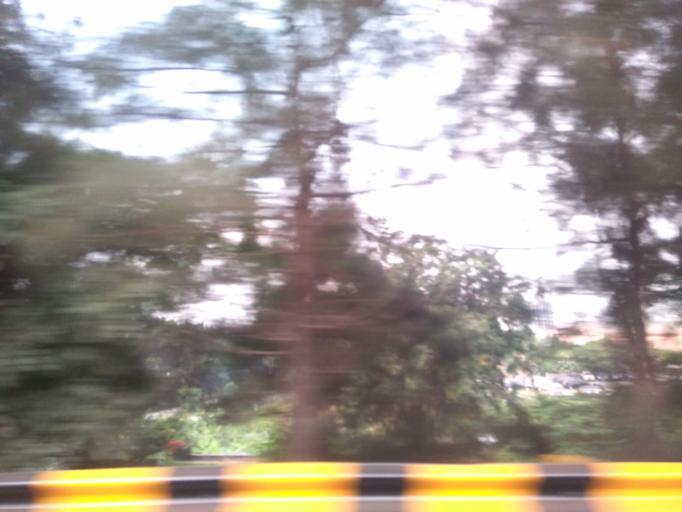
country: ID
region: West Java
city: Bekasi
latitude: -6.2543
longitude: 106.9911
